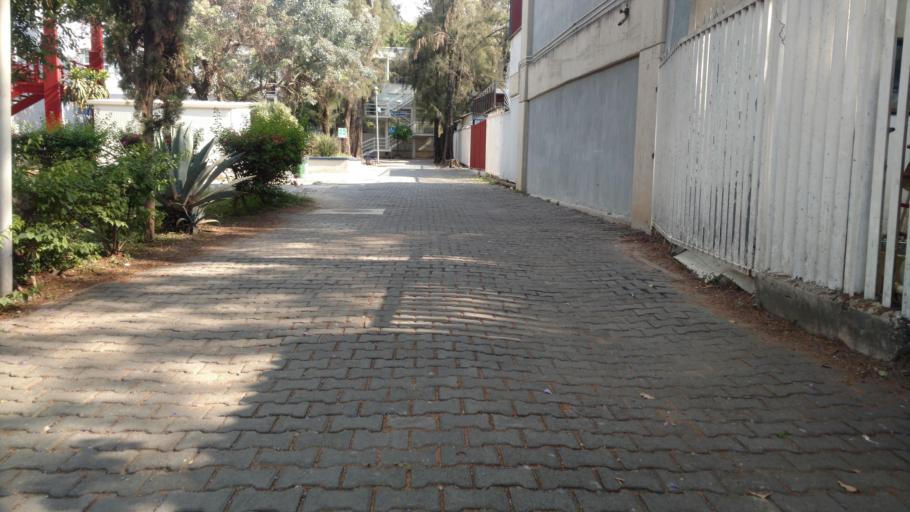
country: MX
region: Jalisco
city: Tlaquepaque
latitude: 20.6567
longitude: -103.3264
